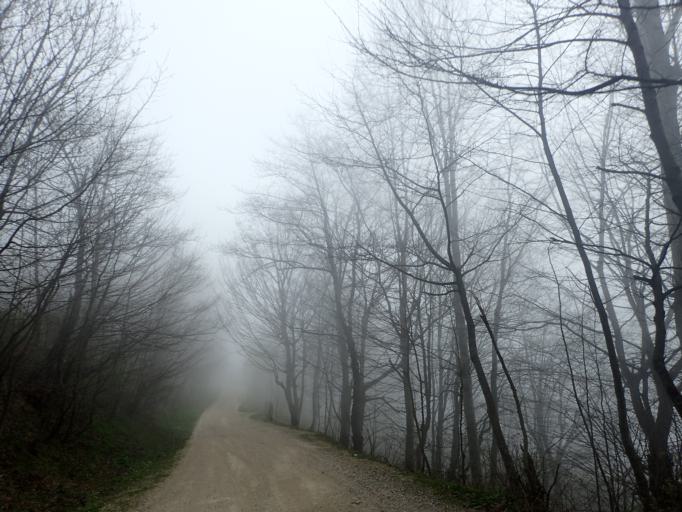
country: TR
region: Ordu
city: Korgan
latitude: 40.7774
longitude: 37.2755
